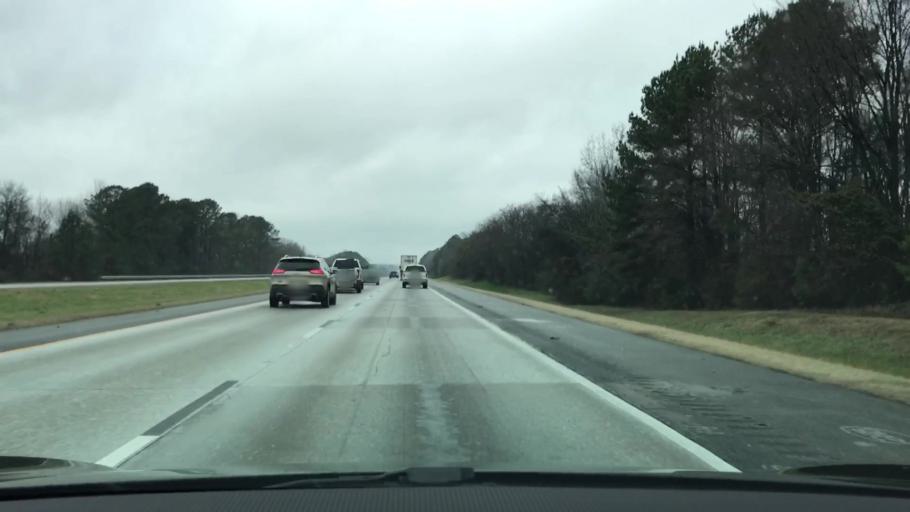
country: US
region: Georgia
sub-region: Putnam County
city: Jefferson
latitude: 33.5420
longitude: -83.3218
